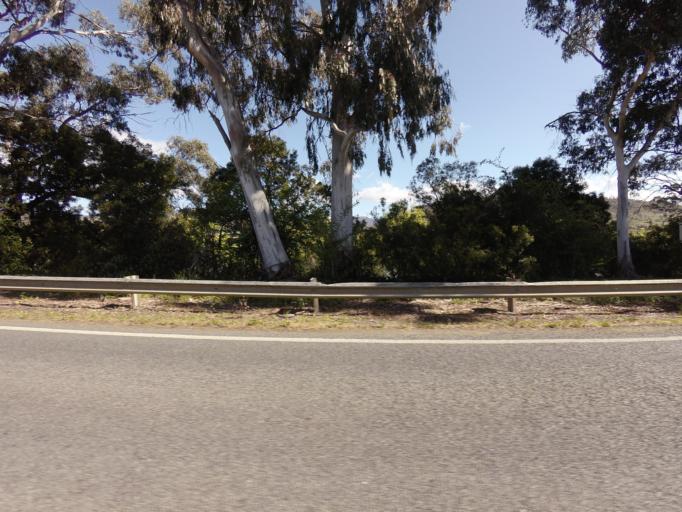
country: AU
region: Tasmania
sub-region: Derwent Valley
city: New Norfolk
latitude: -42.7661
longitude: 147.0224
